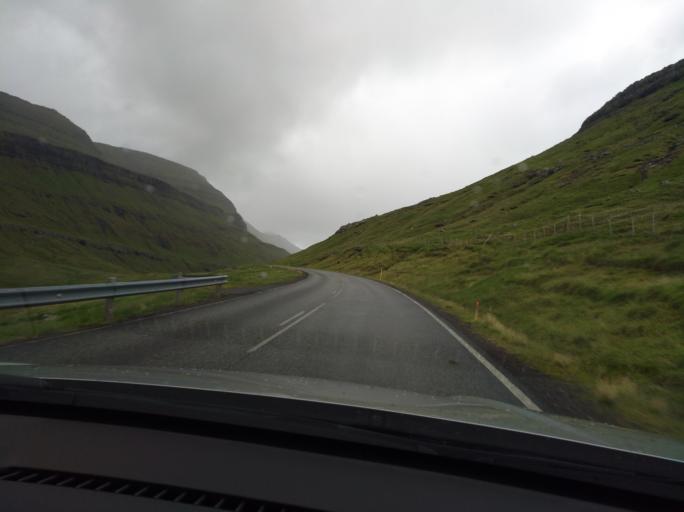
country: FO
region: Eysturoy
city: Fuglafjordur
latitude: 62.2289
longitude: -6.8789
